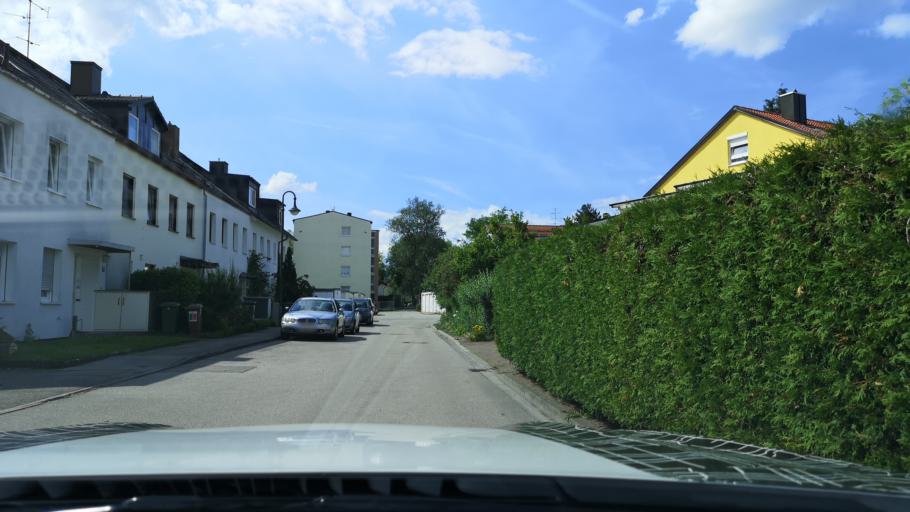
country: DE
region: Bavaria
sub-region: Upper Bavaria
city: Garching bei Munchen
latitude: 48.2460
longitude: 11.6134
